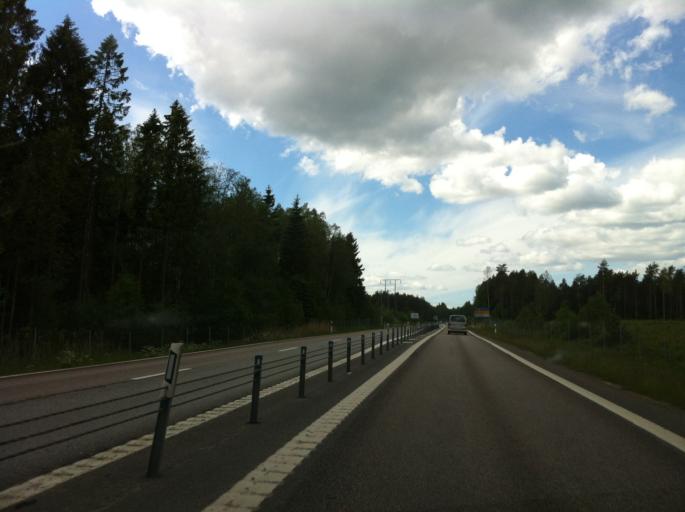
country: SE
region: Vaestra Goetaland
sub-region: Amals Kommun
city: Amal
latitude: 59.1047
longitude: 12.7924
